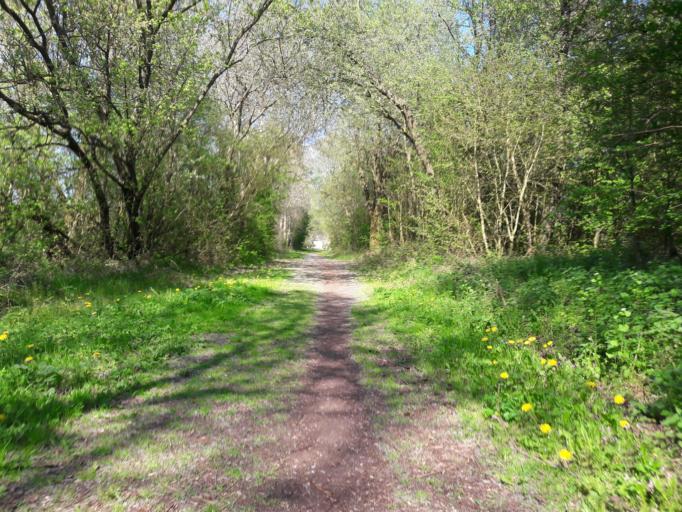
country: FR
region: Nord-Pas-de-Calais
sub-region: Departement du Nord
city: Sains-du-Nord
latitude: 50.1706
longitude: 4.0771
